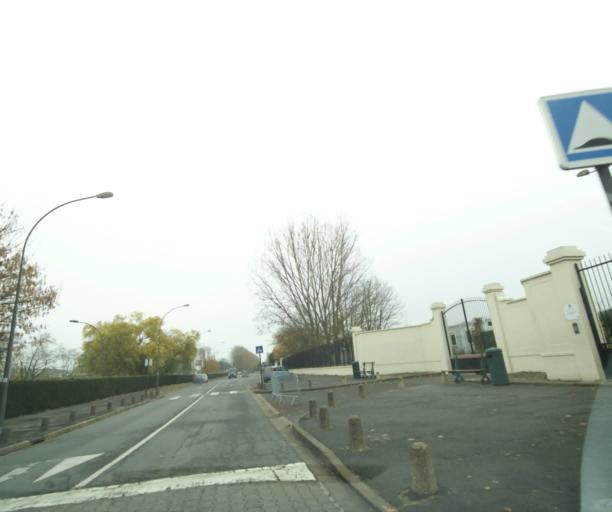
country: FR
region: Ile-de-France
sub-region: Departement de Seine-Saint-Denis
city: Vaujours
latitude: 48.9336
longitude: 2.5689
